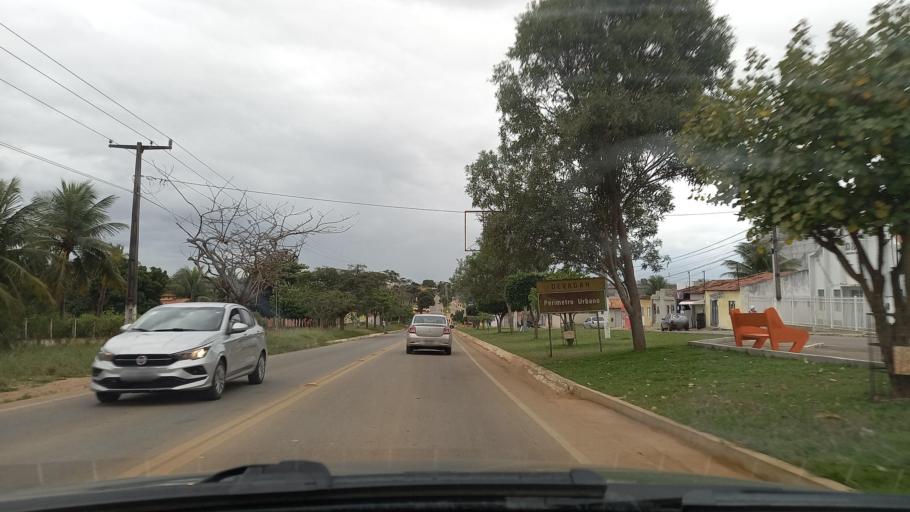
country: BR
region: Sergipe
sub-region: Caninde De Sao Francisco
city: Caninde de Sao Francisco
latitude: -9.6732
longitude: -37.7934
